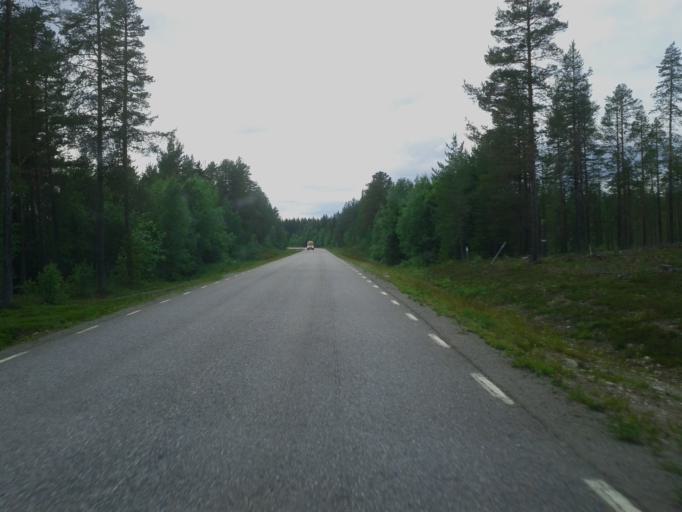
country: SE
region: Vaesterbotten
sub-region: Sorsele Kommun
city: Sorsele
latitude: 65.2898
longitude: 17.8180
